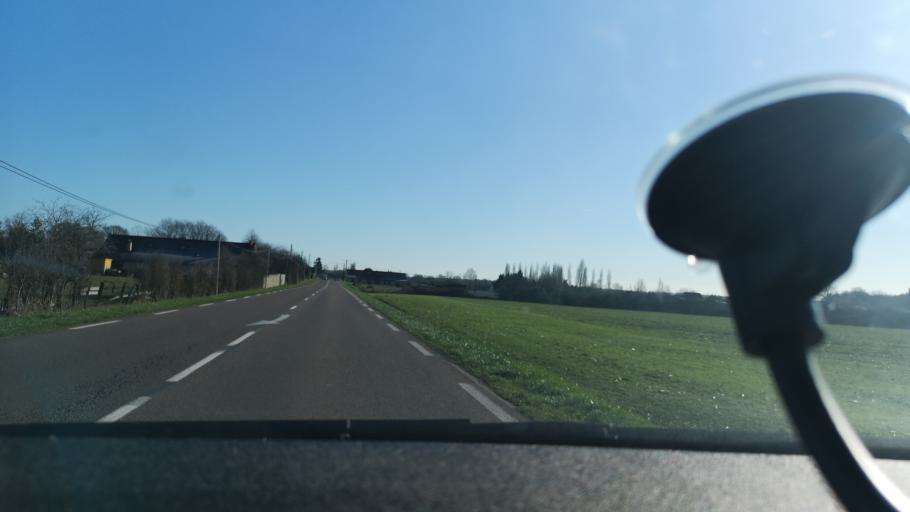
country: FR
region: Bourgogne
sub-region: Departement de Saone-et-Loire
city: Ouroux-sur-Saone
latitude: 46.7642
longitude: 4.9867
